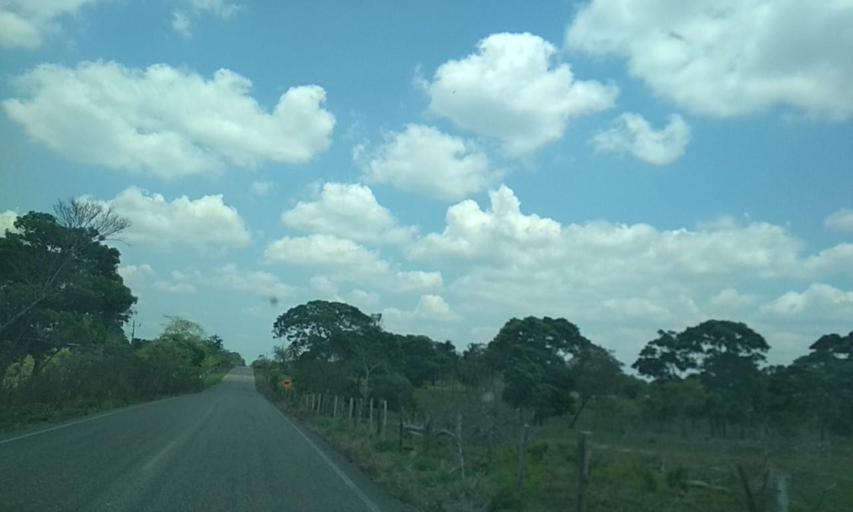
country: MX
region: Tabasco
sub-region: Huimanguillo
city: Huapacal 1ra. Seccion
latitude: 17.7542
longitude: -93.7517
